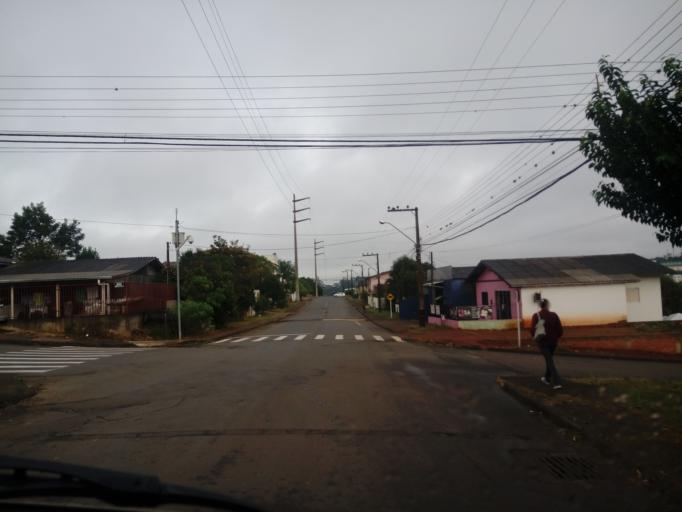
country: BR
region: Santa Catarina
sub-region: Chapeco
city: Chapeco
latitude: -27.0821
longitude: -52.6054
